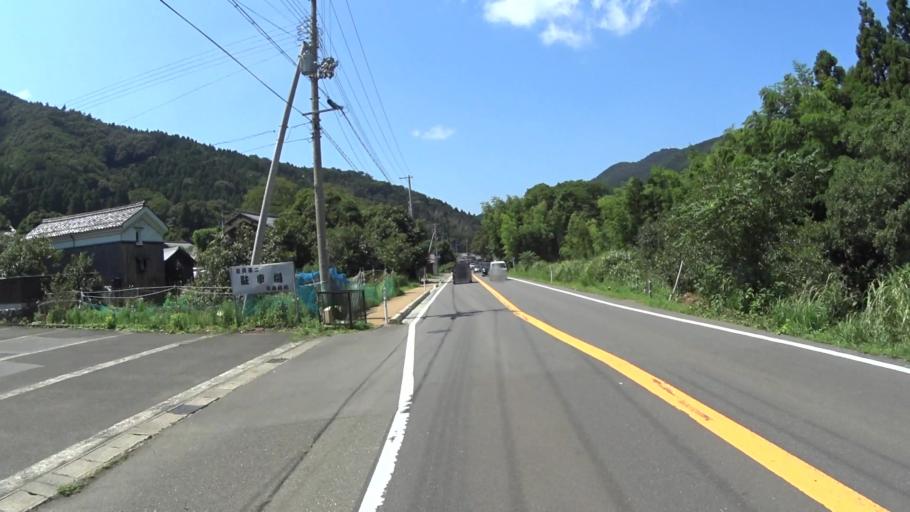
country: JP
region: Fukui
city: Obama
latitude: 35.4435
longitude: 135.9020
